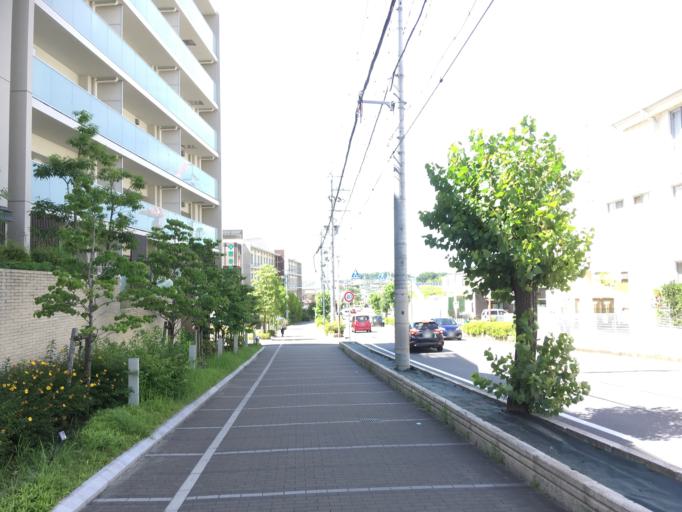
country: JP
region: Nara
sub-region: Ikoma-shi
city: Ikoma
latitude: 34.7028
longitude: 135.7503
